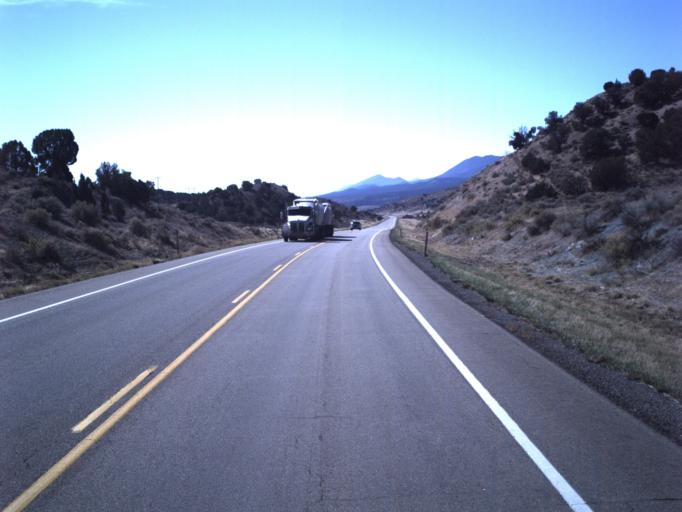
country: US
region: Utah
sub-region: Sanpete County
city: Gunnison
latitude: 39.3785
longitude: -111.9278
